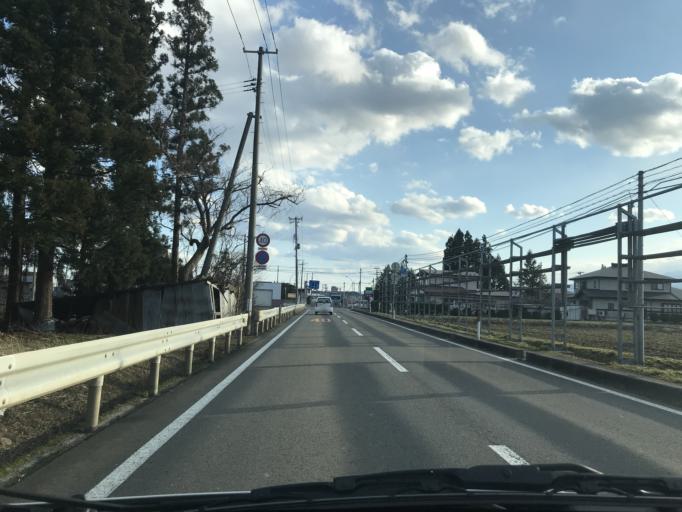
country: JP
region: Iwate
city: Kitakami
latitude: 39.3064
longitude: 141.0340
